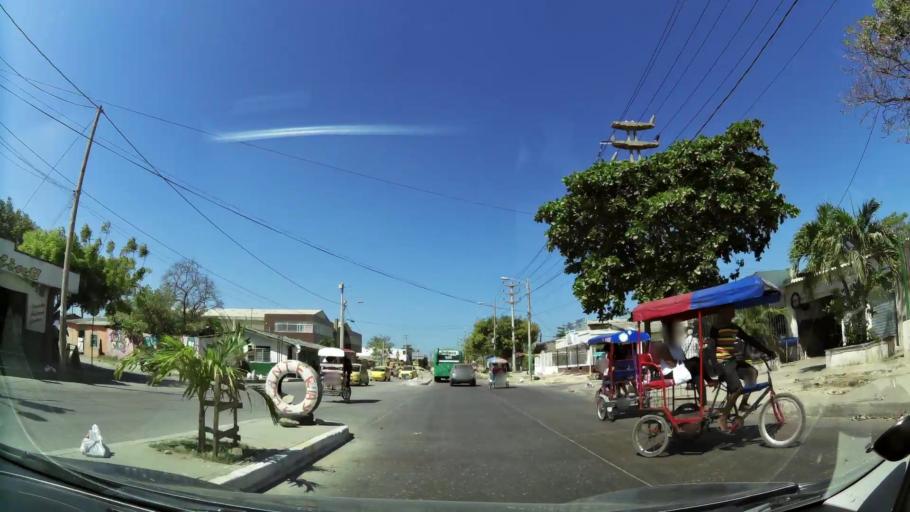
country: CO
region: Atlantico
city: Barranquilla
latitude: 10.9711
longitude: -74.7745
